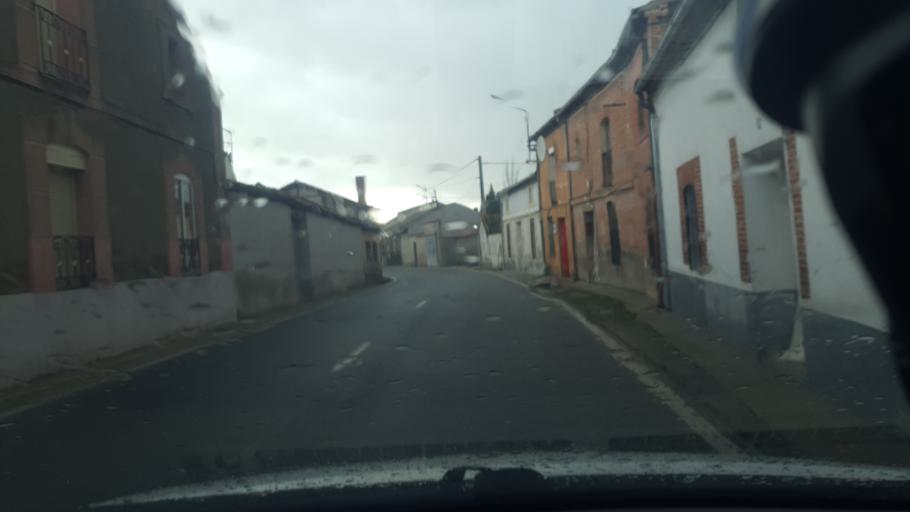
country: ES
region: Castille and Leon
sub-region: Provincia de Segovia
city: Samboal
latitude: 41.2999
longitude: -4.4068
